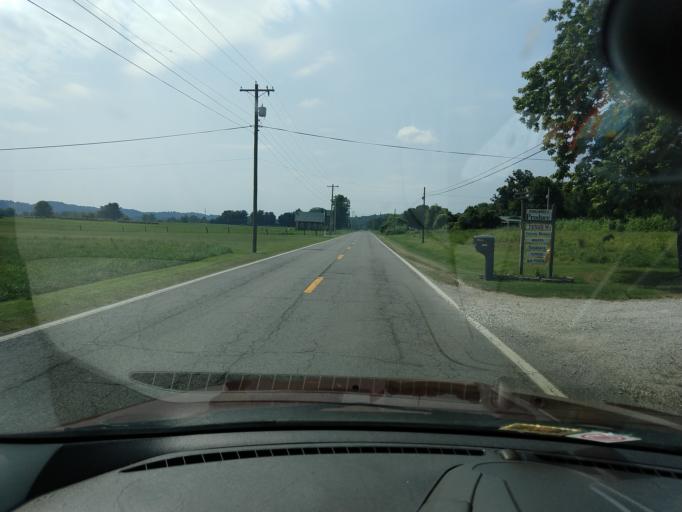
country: US
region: West Virginia
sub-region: Mason County
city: New Haven
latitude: 38.9468
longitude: -81.9204
